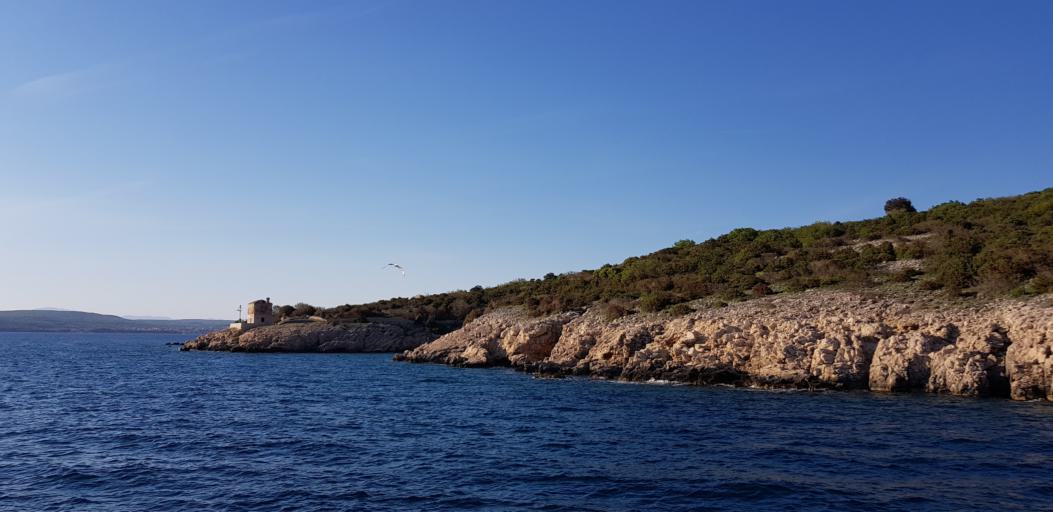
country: HR
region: Primorsko-Goranska
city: Punat
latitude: 44.9775
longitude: 14.6192
